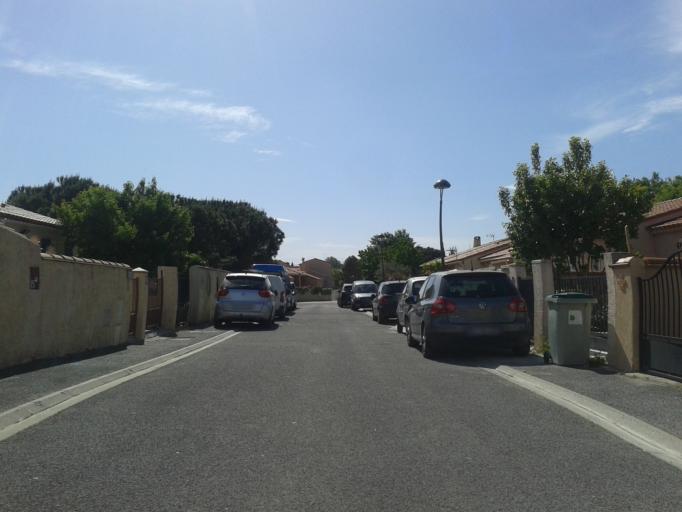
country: FR
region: Languedoc-Roussillon
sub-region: Departement des Pyrenees-Orientales
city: Corneilla-la-Riviere
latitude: 42.7007
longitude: 2.7303
